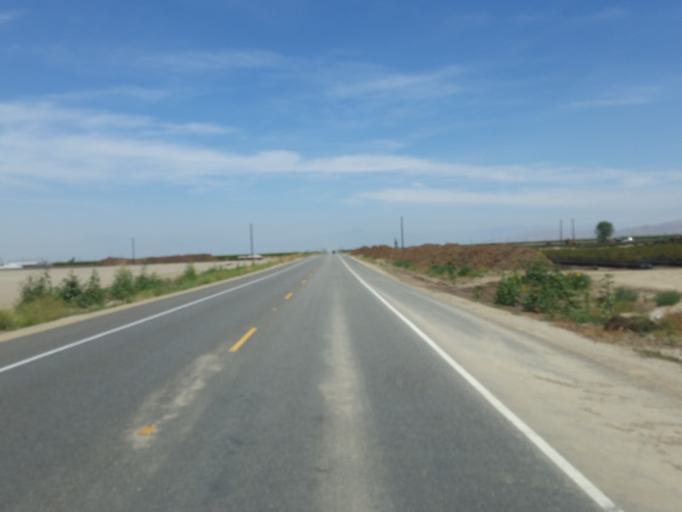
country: US
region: California
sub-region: Kern County
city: Maricopa
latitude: 35.0583
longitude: -119.2229
